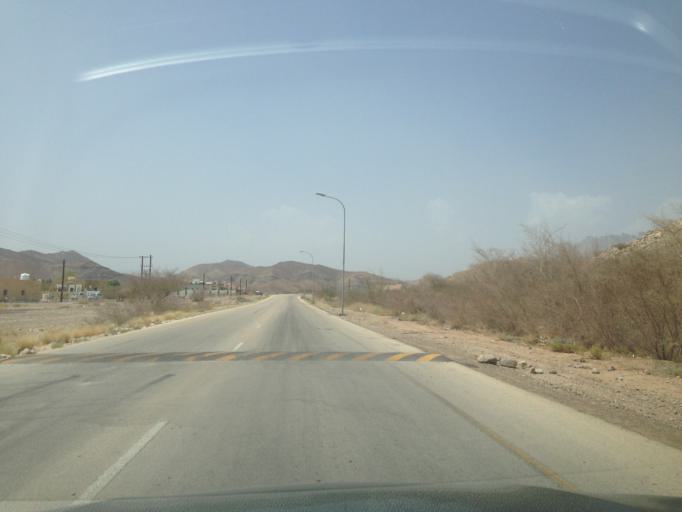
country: OM
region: Az Zahirah
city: `Ibri
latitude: 23.1758
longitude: 56.9187
